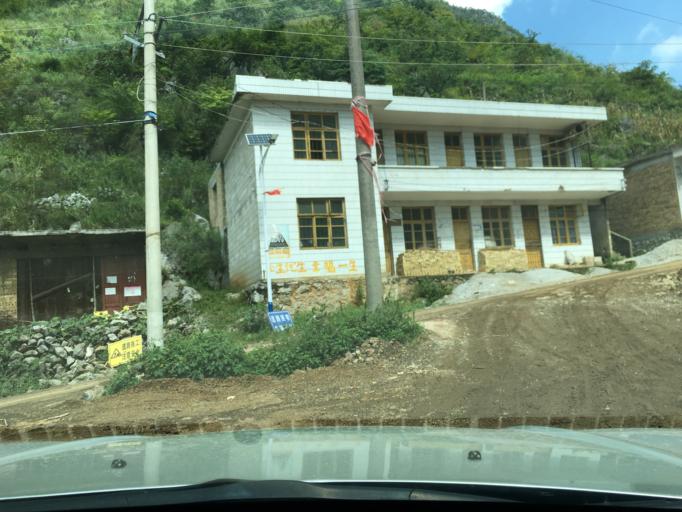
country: CN
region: Guizhou Sheng
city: Liupanshui
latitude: 25.9107
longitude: 105.0995
